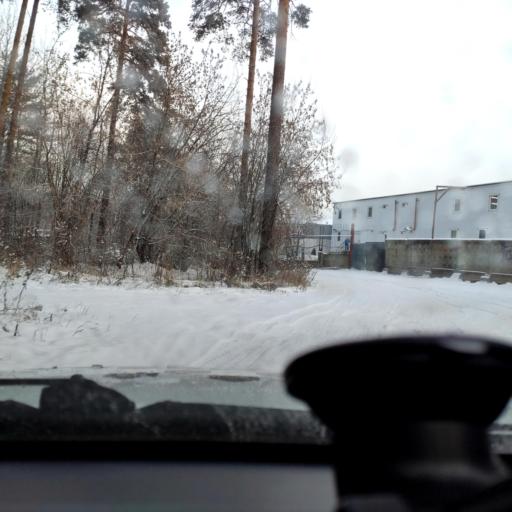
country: RU
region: Perm
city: Kondratovo
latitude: 57.9741
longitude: 56.1493
